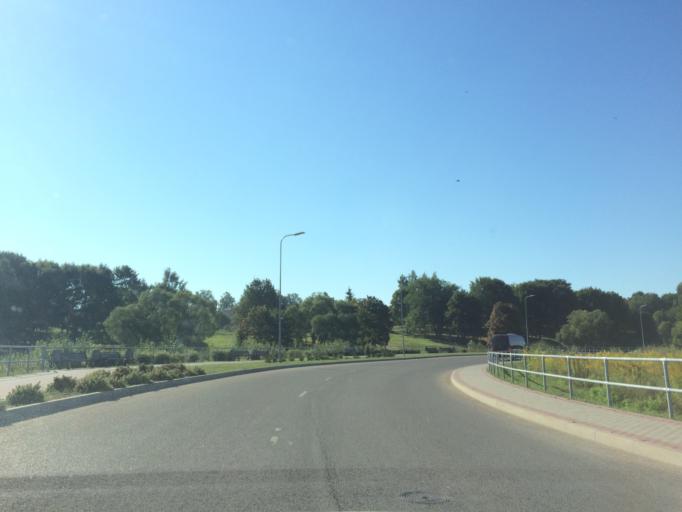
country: LV
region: Rezekne
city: Rezekne
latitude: 56.5121
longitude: 27.3520
